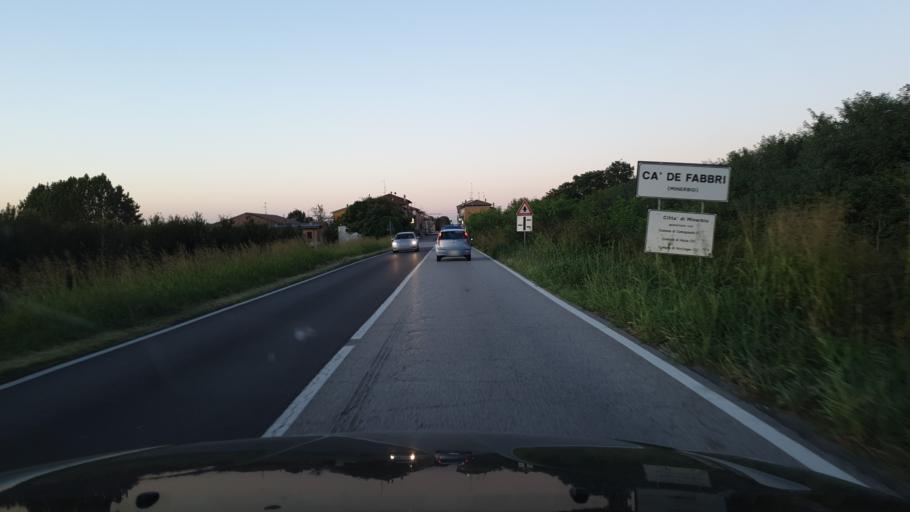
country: IT
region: Emilia-Romagna
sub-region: Provincia di Bologna
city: Ca De Fabbri
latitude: 44.6169
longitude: 11.4519
